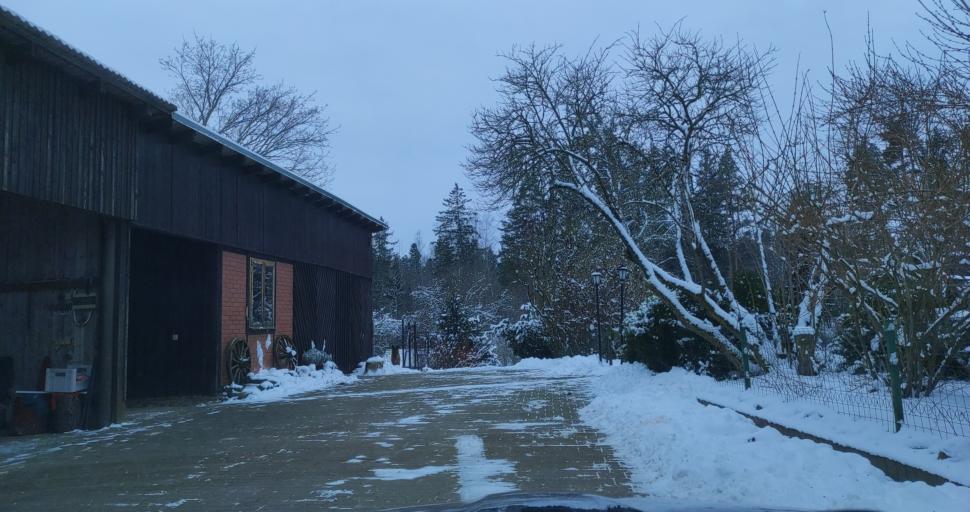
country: LV
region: Alsunga
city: Alsunga
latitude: 56.9554
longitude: 21.6017
